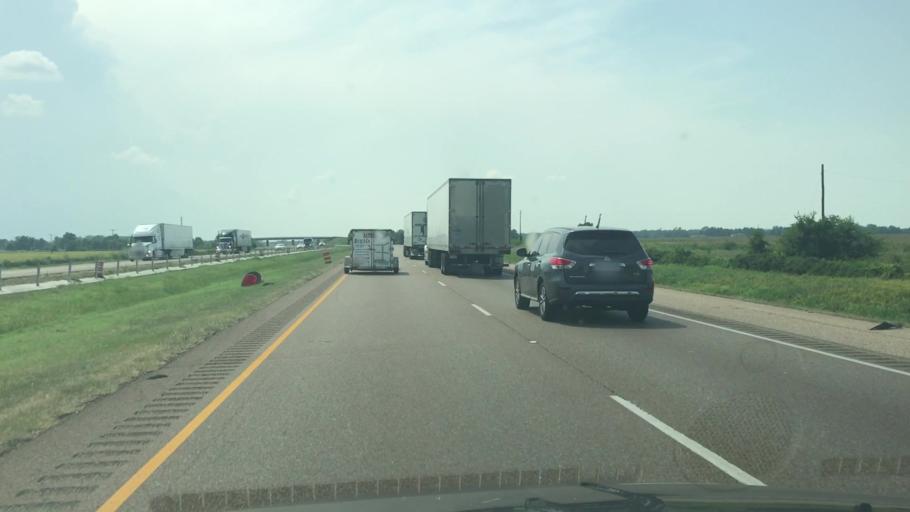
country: US
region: Arkansas
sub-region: Crittenden County
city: Earle
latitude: 35.1513
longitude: -90.3924
